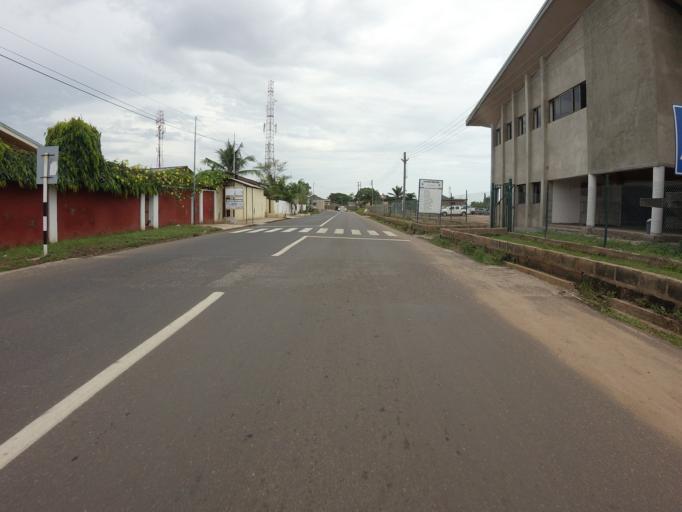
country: GH
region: Greater Accra
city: Accra
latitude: 5.6033
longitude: -0.2146
